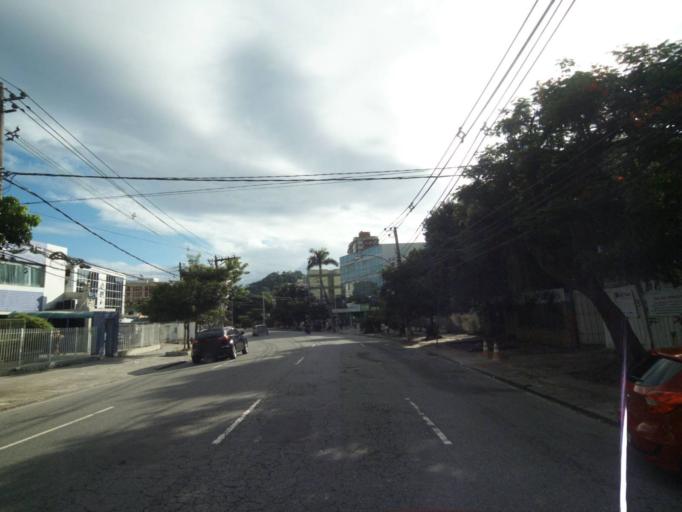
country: BR
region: Rio de Janeiro
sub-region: Rio De Janeiro
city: Rio de Janeiro
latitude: -22.9376
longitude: -43.3382
